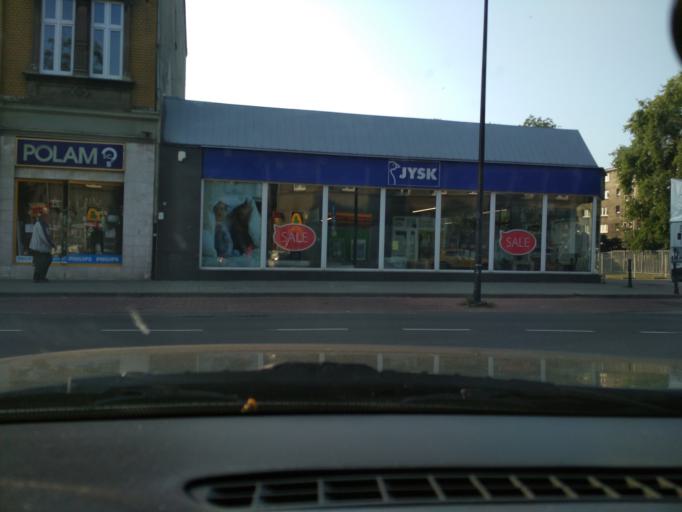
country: PL
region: Silesian Voivodeship
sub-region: Gliwice
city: Gliwice
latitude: 50.2965
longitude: 18.6748
